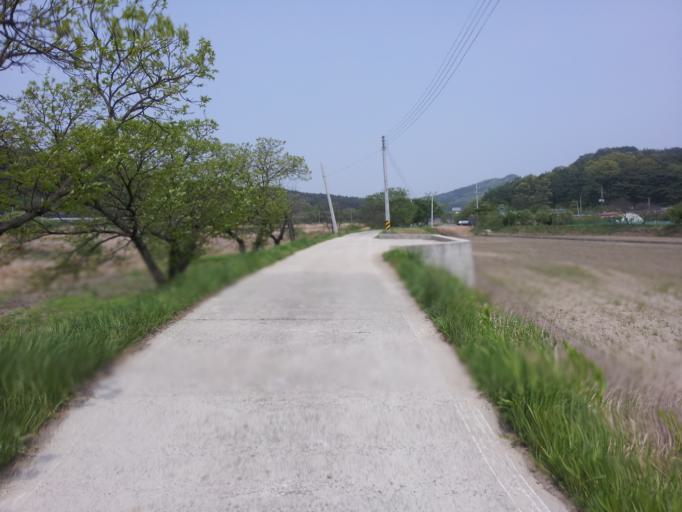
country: KR
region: Daejeon
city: Daejeon
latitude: 36.2581
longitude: 127.2828
